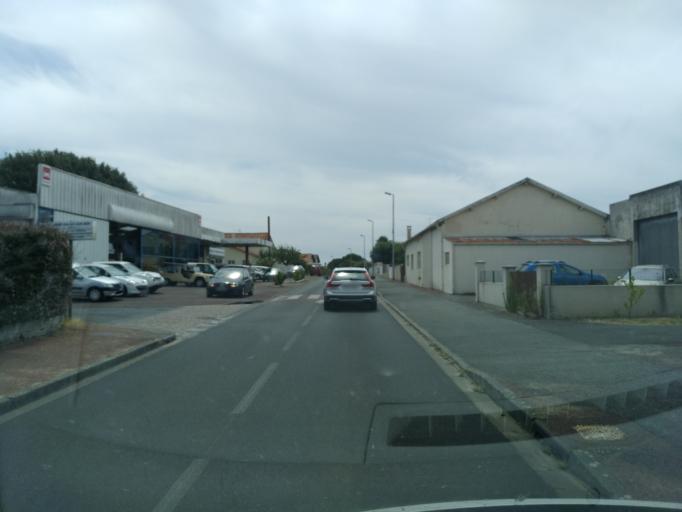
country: FR
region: Poitou-Charentes
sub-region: Departement de la Charente-Maritime
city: Saint-Palais-sur-Mer
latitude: 45.6469
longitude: -1.0836
